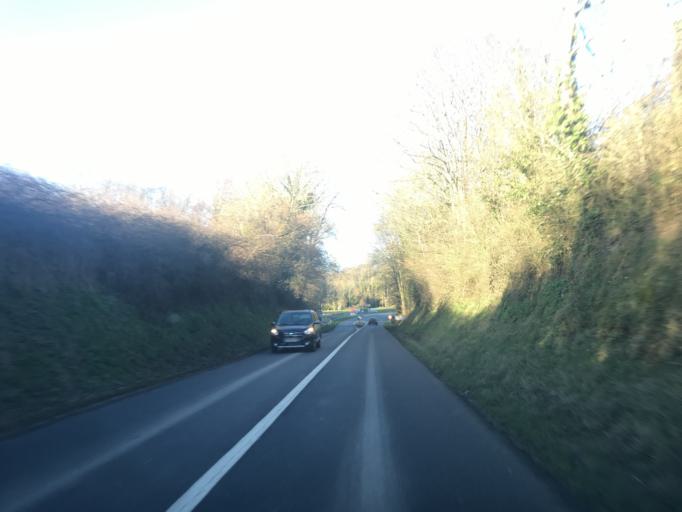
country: FR
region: Lower Normandy
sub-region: Departement du Calvados
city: Beuville
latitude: 49.2253
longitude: -0.3351
